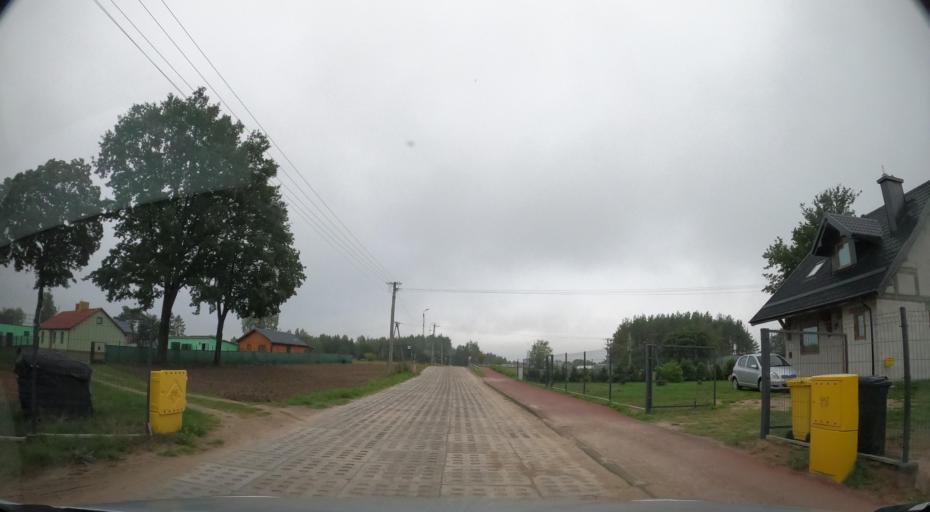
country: PL
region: Pomeranian Voivodeship
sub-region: Powiat kartuski
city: Chwaszczyno
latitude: 54.4280
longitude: 18.4160
